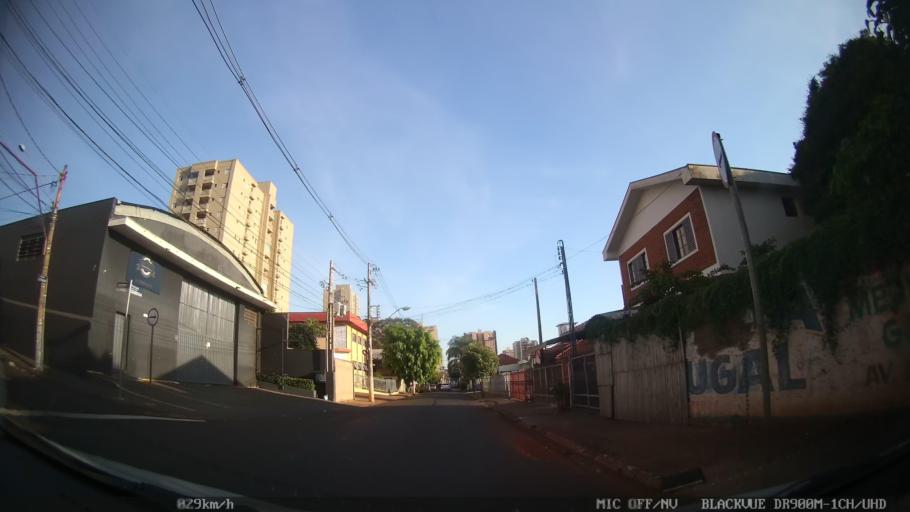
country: BR
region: Sao Paulo
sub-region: Ribeirao Preto
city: Ribeirao Preto
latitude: -21.2053
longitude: -47.7939
